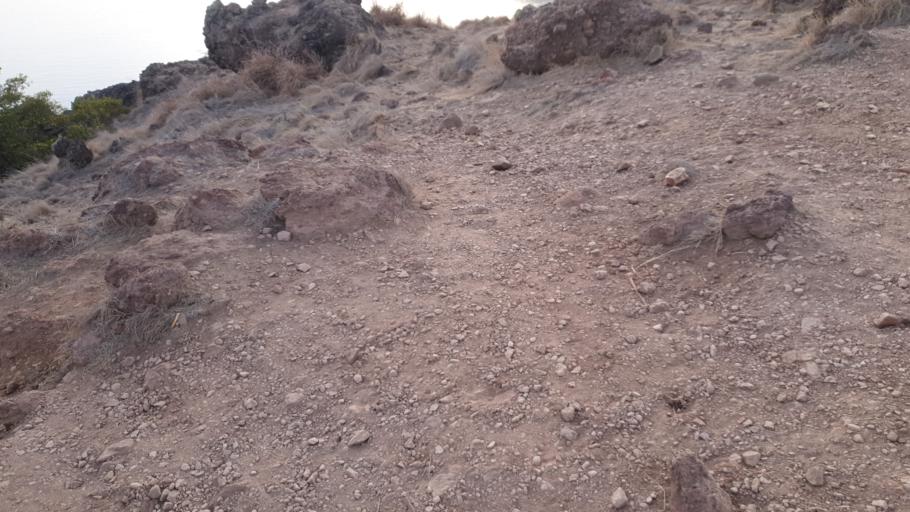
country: ID
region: East Nusa Tenggara
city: Komodo
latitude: -8.6812
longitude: 119.5572
